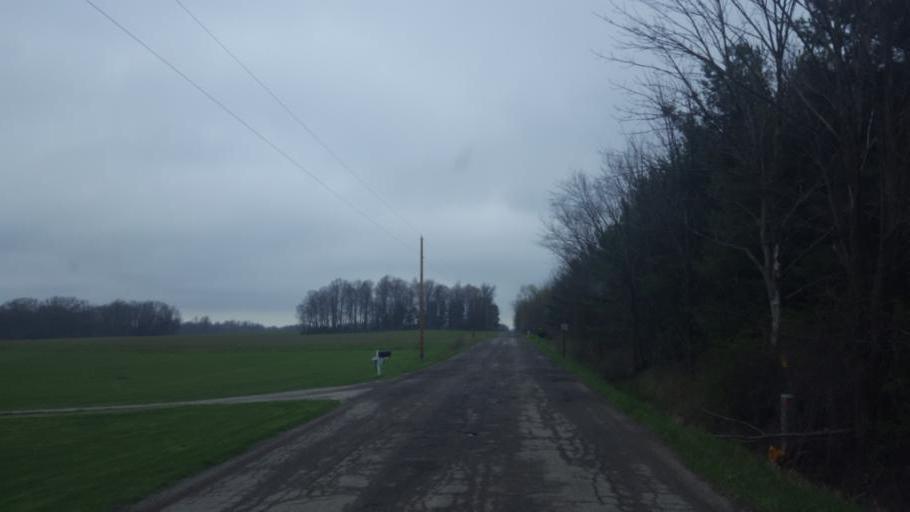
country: US
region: Ohio
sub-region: Crawford County
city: Galion
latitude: 40.6827
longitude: -82.7464
